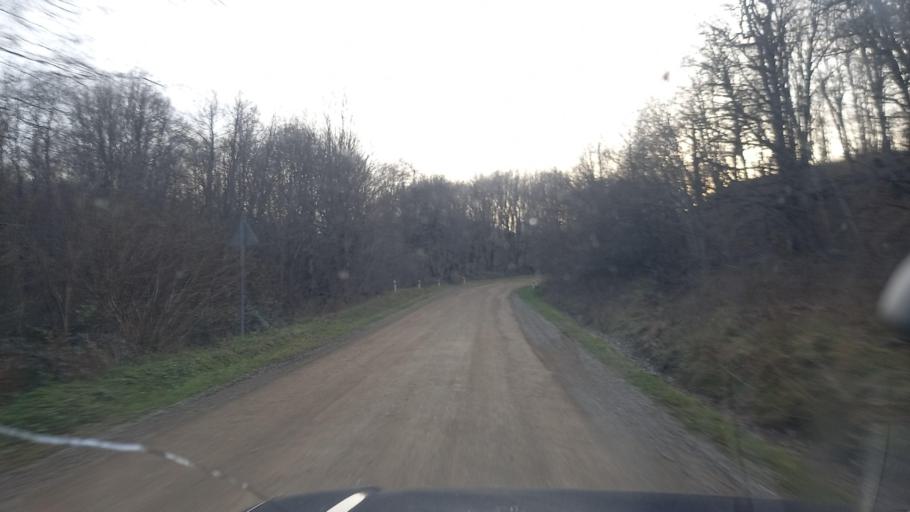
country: RU
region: Krasnodarskiy
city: Khadyzhensk
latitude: 44.3378
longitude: 39.2803
